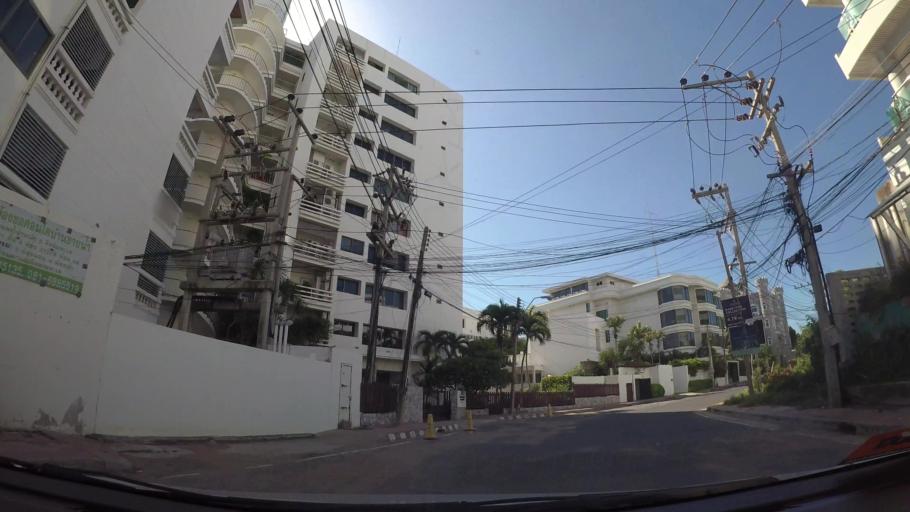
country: TH
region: Chon Buri
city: Phatthaya
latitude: 12.9105
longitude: 100.8567
